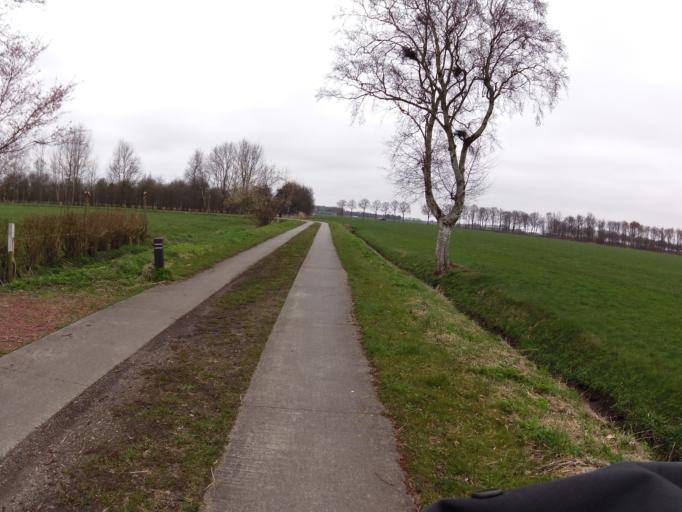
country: NL
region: Drenthe
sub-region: Gemeente Westerveld
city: Dwingeloo
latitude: 52.9646
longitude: 6.3562
